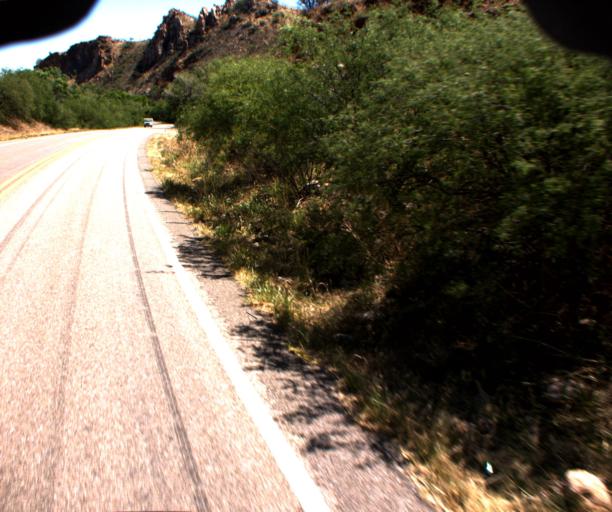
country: US
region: Arizona
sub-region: Santa Cruz County
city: Rio Rico
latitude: 31.5057
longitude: -110.8067
